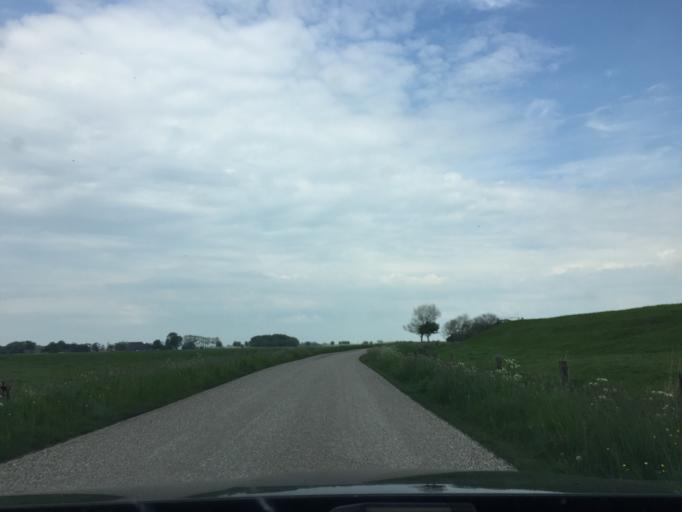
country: NL
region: Groningen
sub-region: Gemeente De Marne
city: Ulrum
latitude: 53.3374
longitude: 6.3455
